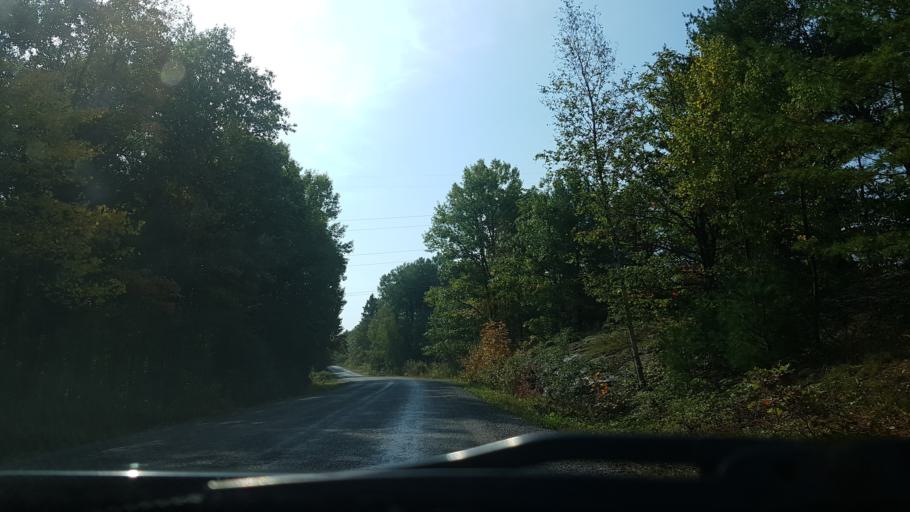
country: CA
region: Ontario
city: Gravenhurst
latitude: 44.8059
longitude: -79.2106
